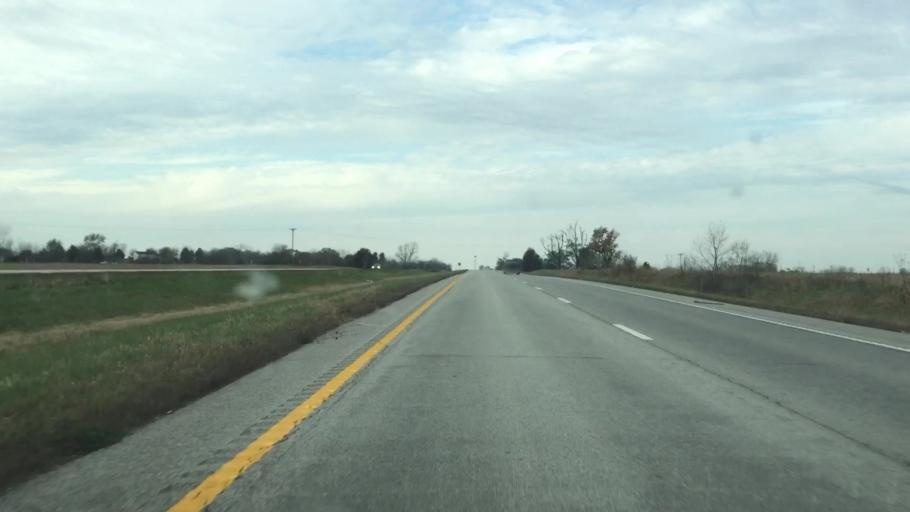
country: US
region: Missouri
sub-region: Cass County
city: Garden City
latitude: 38.5349
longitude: -94.1552
